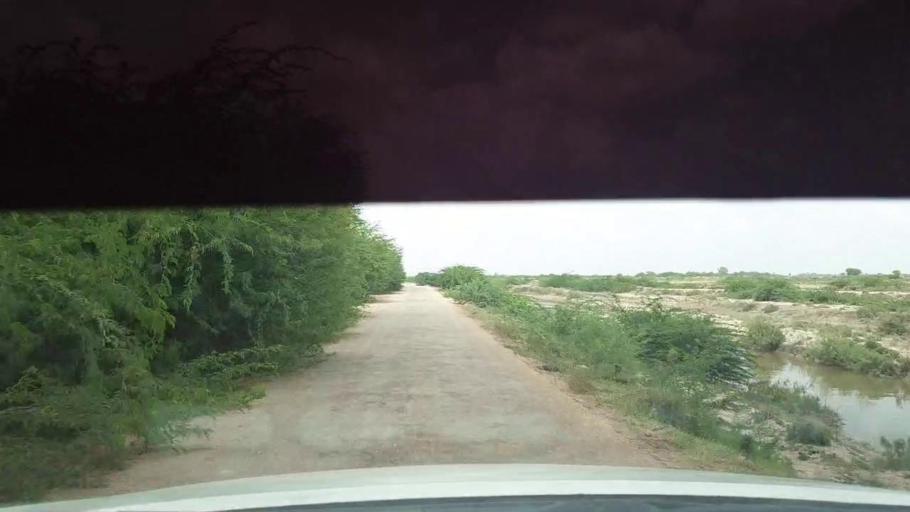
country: PK
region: Sindh
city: Kadhan
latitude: 24.4824
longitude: 69.0664
